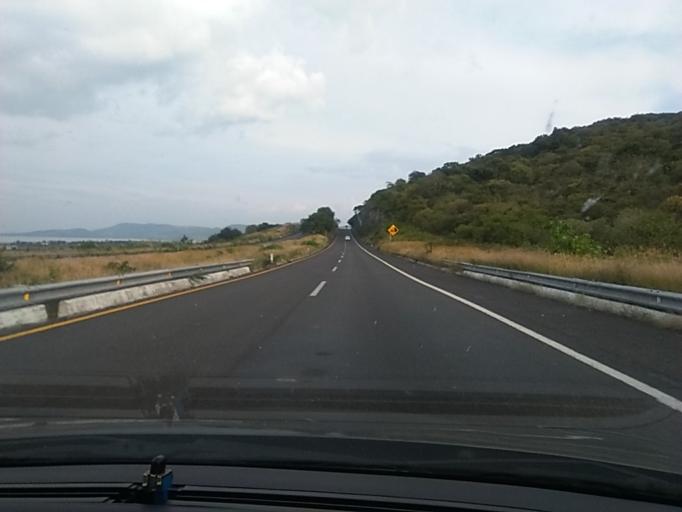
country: MX
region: Michoacan
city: Copandaro de Galeana
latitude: 19.8990
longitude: -101.2606
